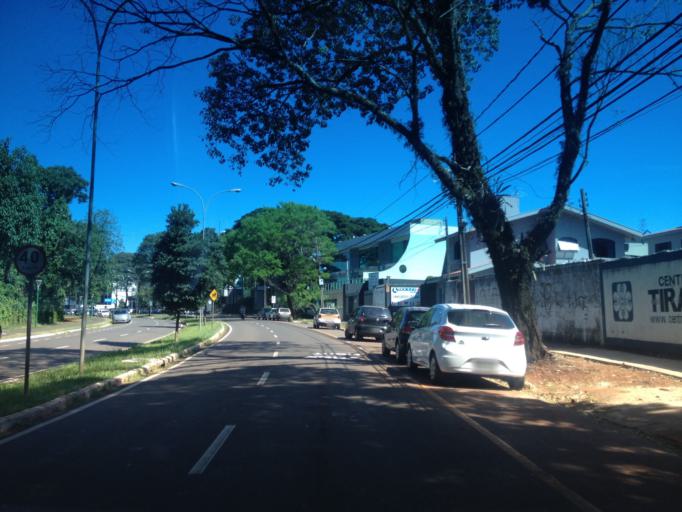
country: BR
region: Parana
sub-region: Maringa
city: Maringa
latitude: -23.4266
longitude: -51.9461
